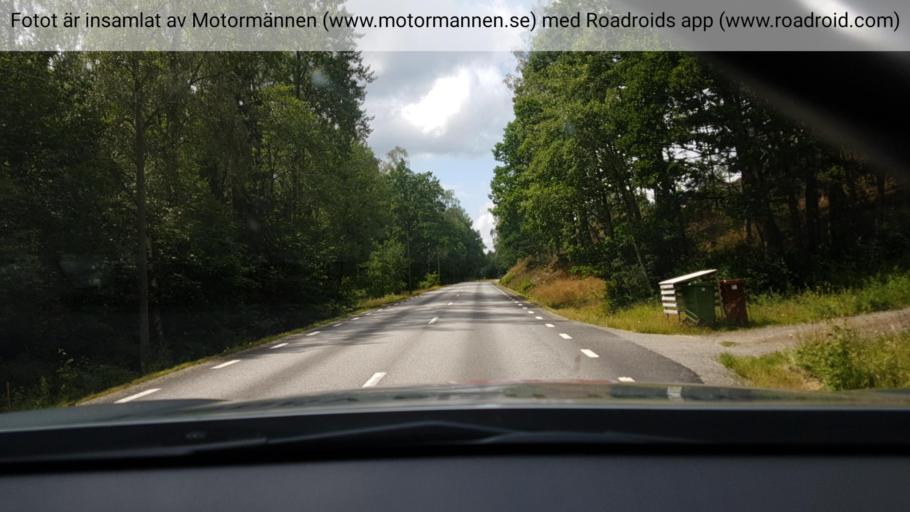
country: SE
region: Vaestra Goetaland
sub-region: Tranemo Kommun
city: Tranemo
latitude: 57.4717
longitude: 13.2505
